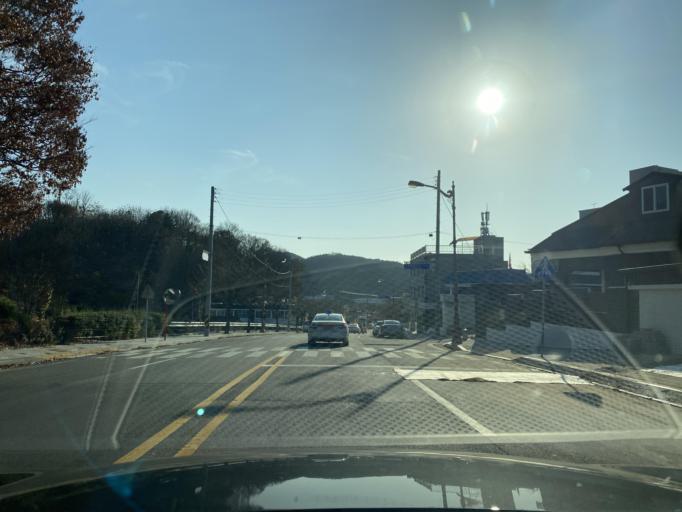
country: KR
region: Chungcheongnam-do
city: Yesan
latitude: 36.6836
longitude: 126.8356
